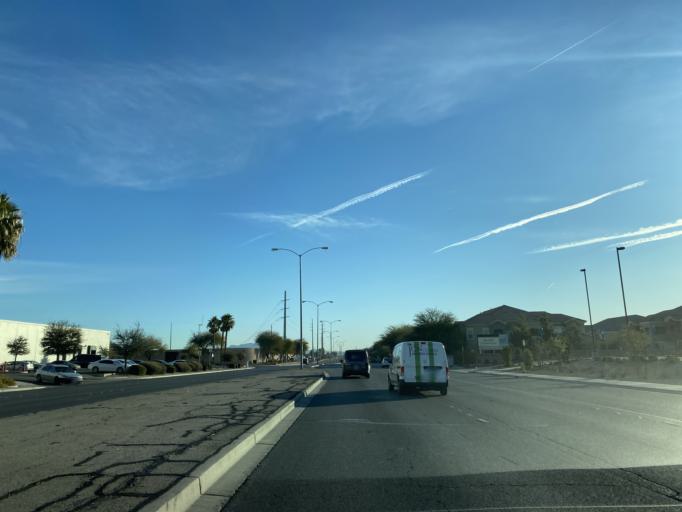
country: US
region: Nevada
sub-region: Clark County
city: Nellis Air Force Base
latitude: 36.2403
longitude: -115.0877
